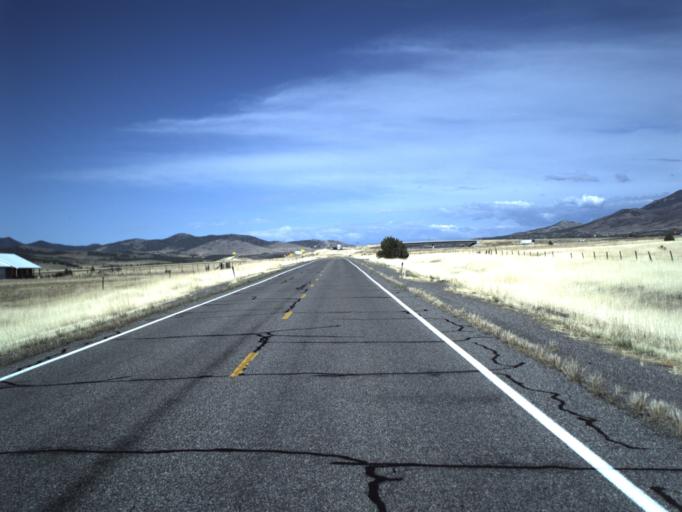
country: US
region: Utah
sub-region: Millard County
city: Fillmore
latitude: 39.1387
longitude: -112.2430
